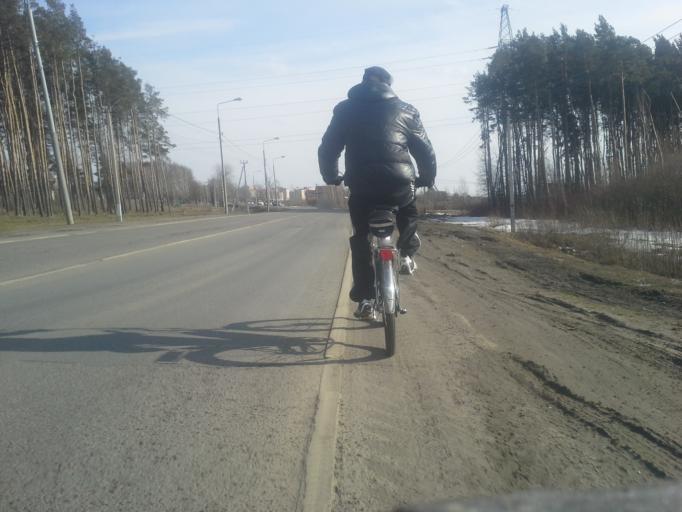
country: RU
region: Moskovskaya
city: Shcherbinka
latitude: 55.4813
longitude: 37.5225
